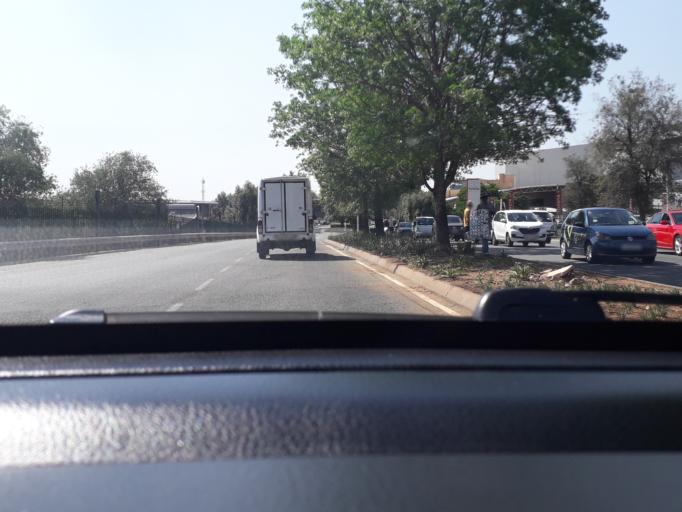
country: ZA
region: Gauteng
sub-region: City of Johannesburg Metropolitan Municipality
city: Modderfontein
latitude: -26.1187
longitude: 28.1377
